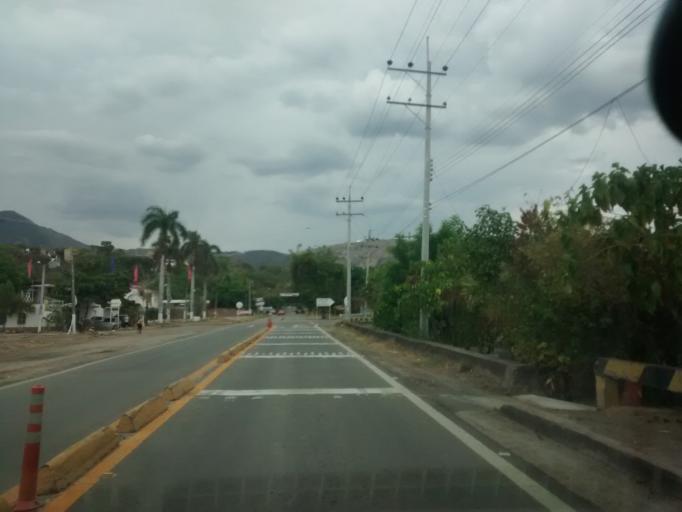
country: CO
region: Cundinamarca
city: Tocaima
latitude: 4.4550
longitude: -74.6450
